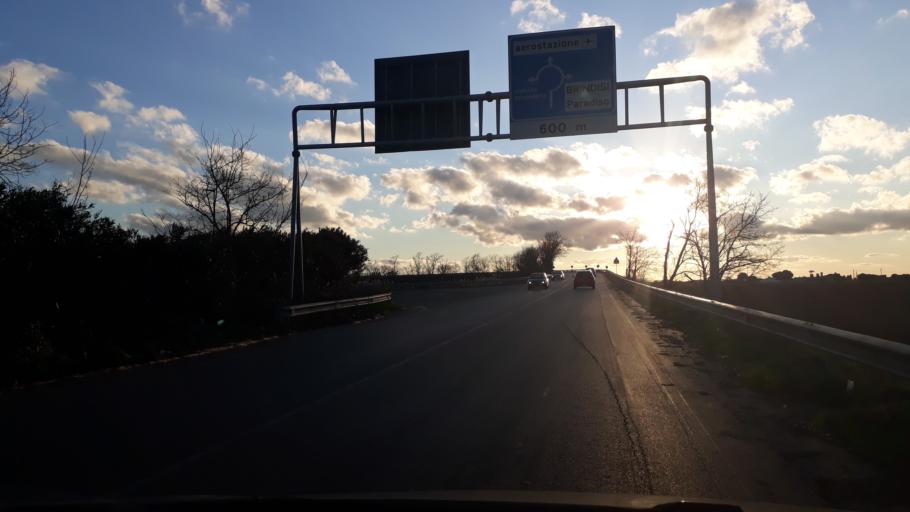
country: IT
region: Apulia
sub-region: Provincia di Brindisi
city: Brindisi
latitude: 40.6547
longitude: 17.8982
